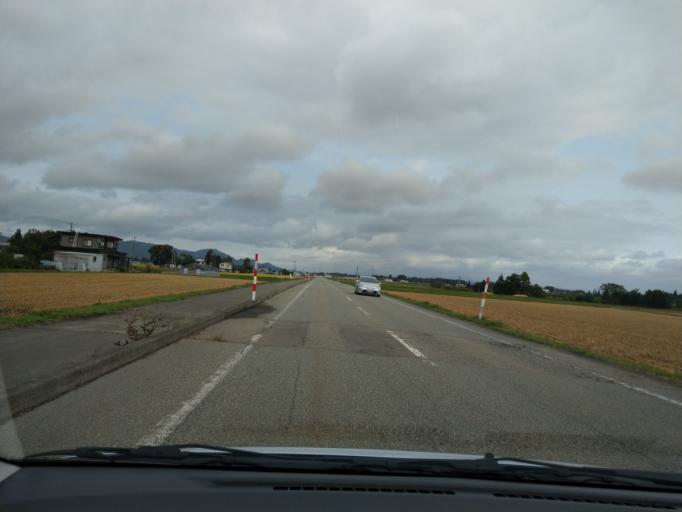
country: JP
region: Akita
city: Omagari
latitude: 39.3867
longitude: 140.4858
